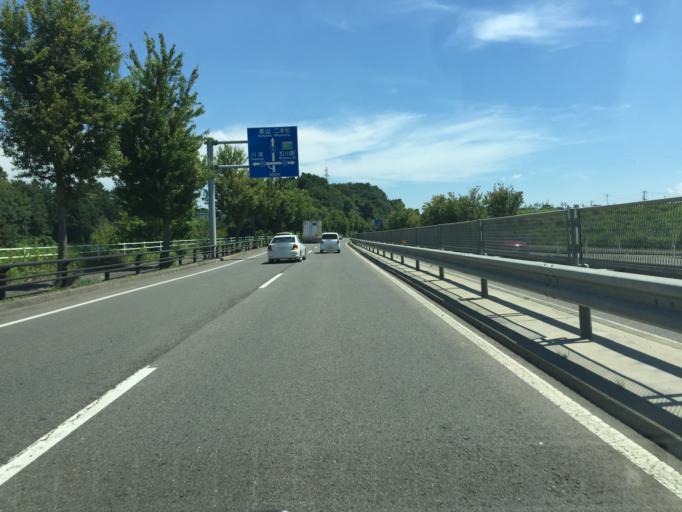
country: JP
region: Fukushima
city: Fukushima-shi
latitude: 37.6610
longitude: 140.4902
